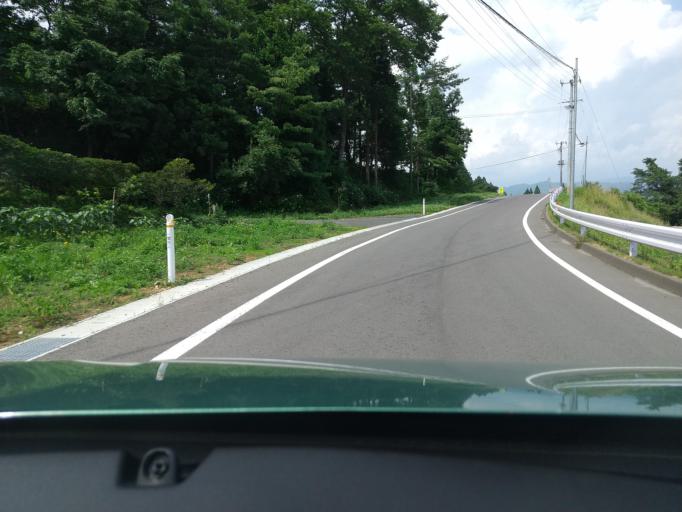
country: JP
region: Iwate
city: Ichinoseki
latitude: 39.0025
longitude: 141.2175
